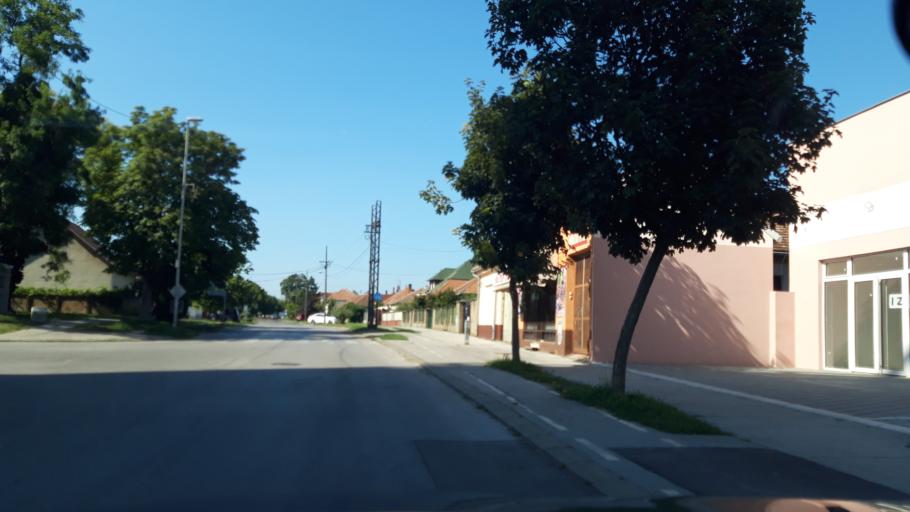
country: RS
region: Autonomna Pokrajina Vojvodina
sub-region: Sremski Okrug
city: Ruma
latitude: 45.0146
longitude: 19.8225
